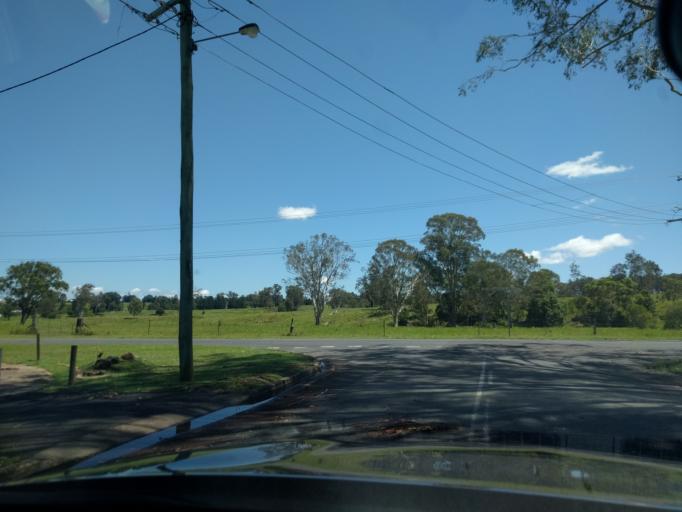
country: AU
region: Queensland
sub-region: Logan
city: Cedar Vale
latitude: -27.9850
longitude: 153.0077
